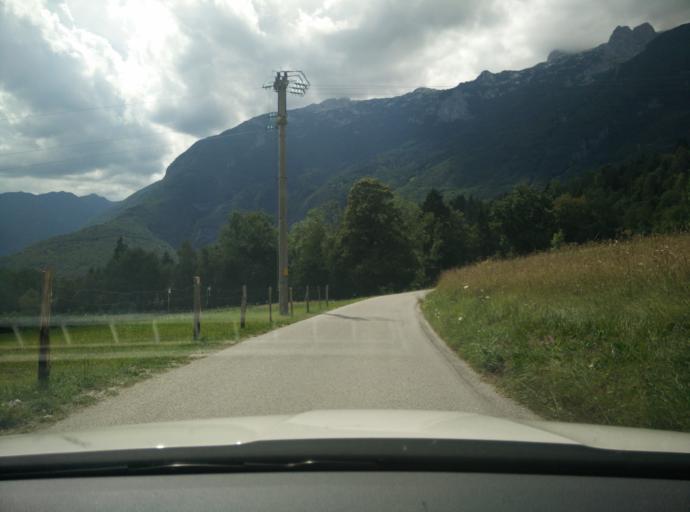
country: SI
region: Bovec
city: Bovec
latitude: 46.3388
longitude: 13.5343
